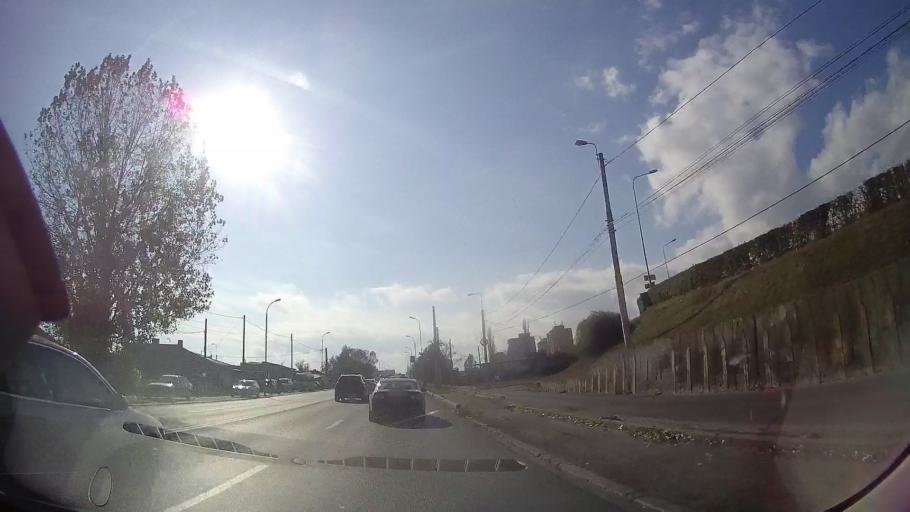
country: RO
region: Constanta
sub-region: Municipiul Constanta
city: Constanta
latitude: 44.1513
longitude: 28.6273
